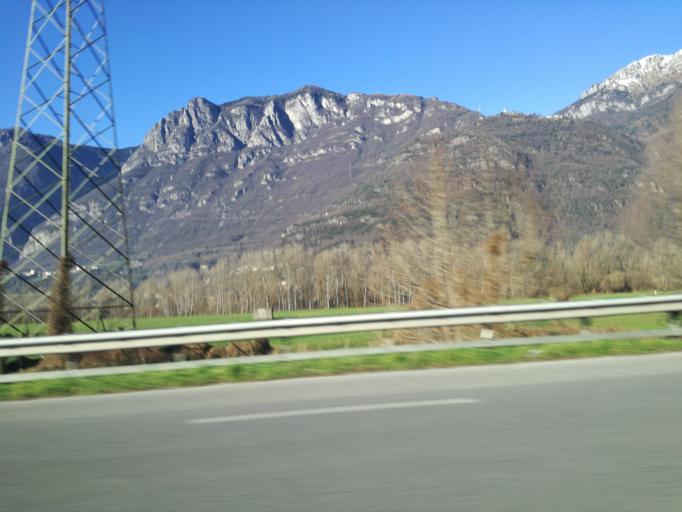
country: IT
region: Lombardy
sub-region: Provincia di Brescia
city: Pian Camuno
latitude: 45.8460
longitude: 10.1365
